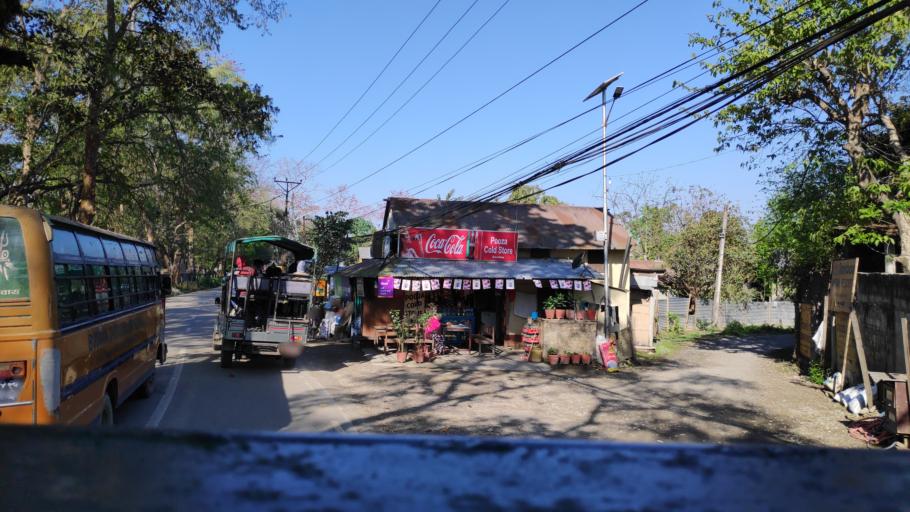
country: NP
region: Central Region
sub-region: Narayani Zone
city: Bharatpur
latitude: 27.5745
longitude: 84.4990
